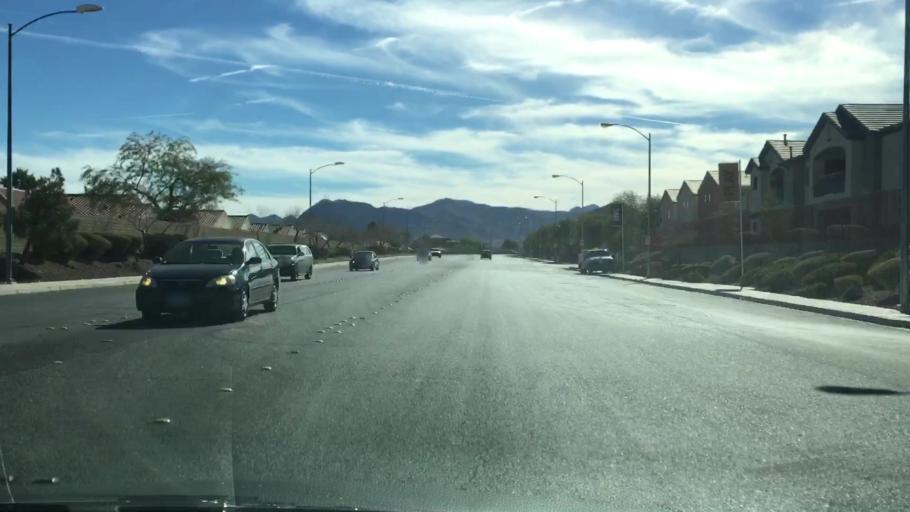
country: US
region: Nevada
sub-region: Clark County
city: Henderson
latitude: 36.0806
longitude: -115.0205
